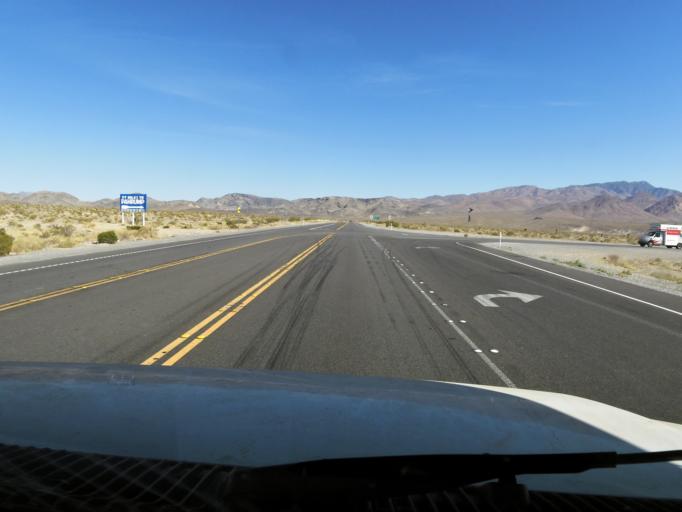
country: US
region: Nevada
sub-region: Nye County
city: Pahrump
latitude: 36.5649
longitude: -116.1240
